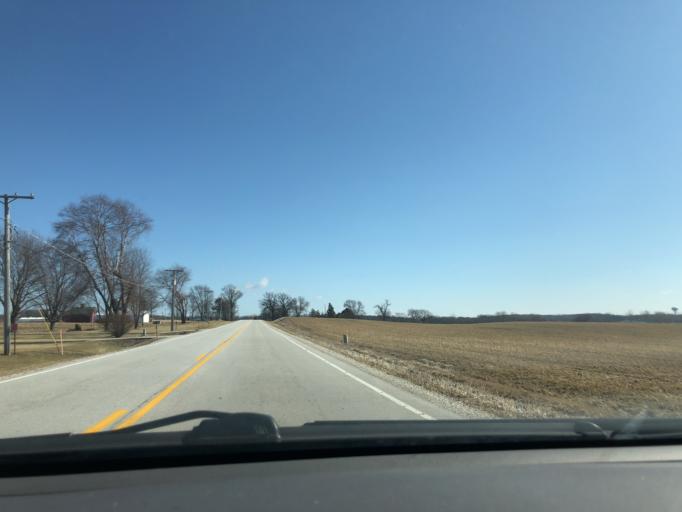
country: US
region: Illinois
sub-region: Kane County
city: Hampshire
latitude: 42.1065
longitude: -88.5210
